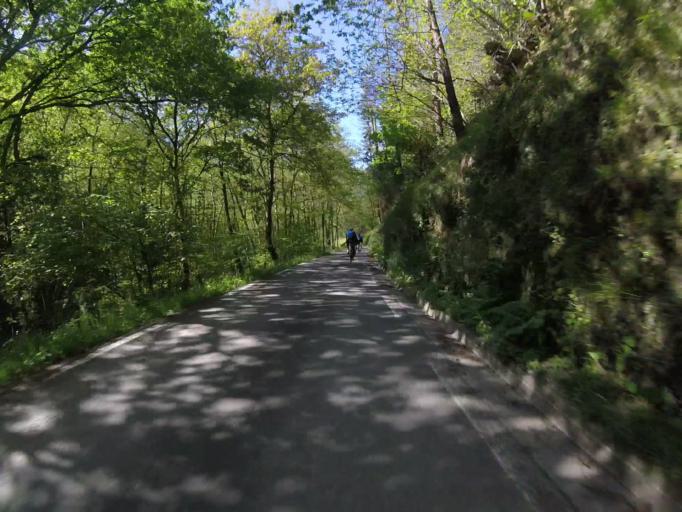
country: ES
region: Basque Country
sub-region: Provincia de Guipuzcoa
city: Errezil
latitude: 43.1803
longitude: -2.2033
